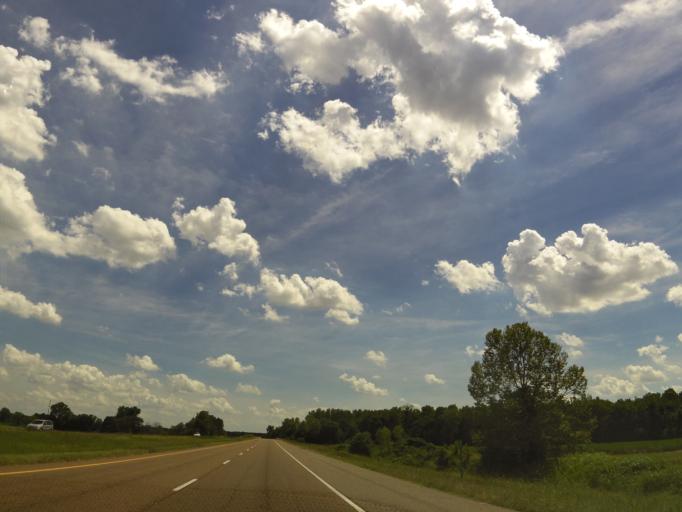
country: US
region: Tennessee
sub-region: Dyer County
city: Dyersburg
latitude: 36.0391
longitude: -89.3381
